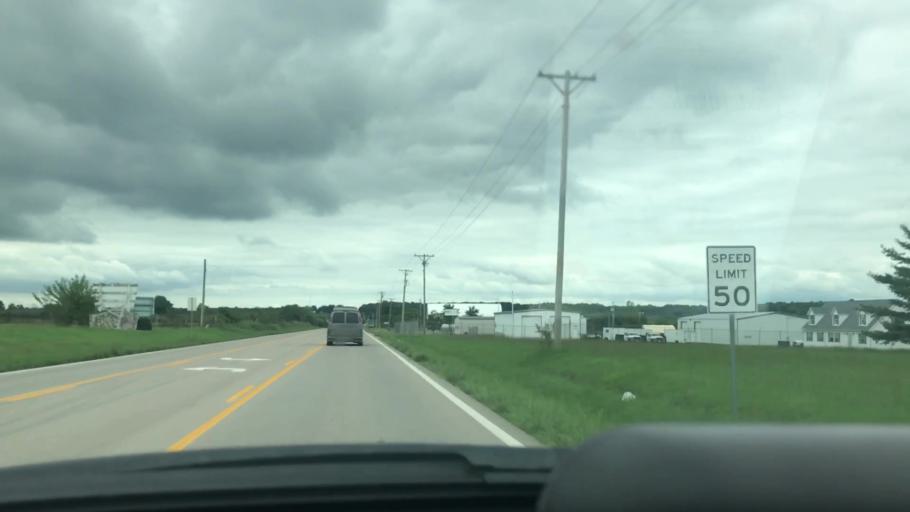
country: US
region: Missouri
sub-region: Dallas County
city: Buffalo
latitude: 37.6577
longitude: -93.1037
